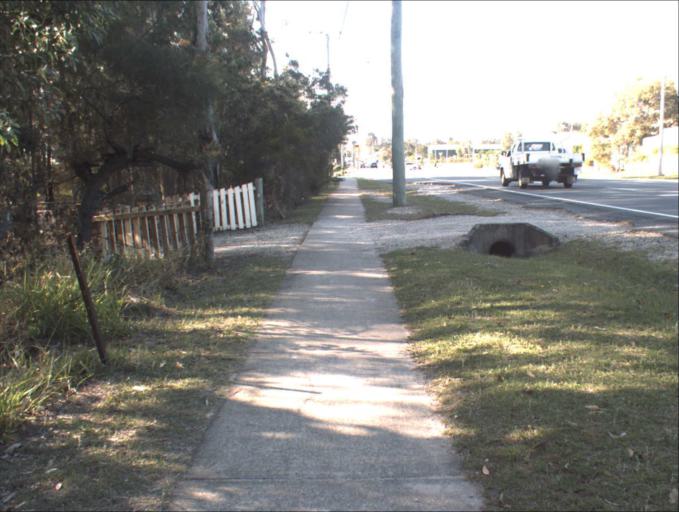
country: AU
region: Queensland
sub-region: Logan
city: Logan City
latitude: -27.6784
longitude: 153.0891
